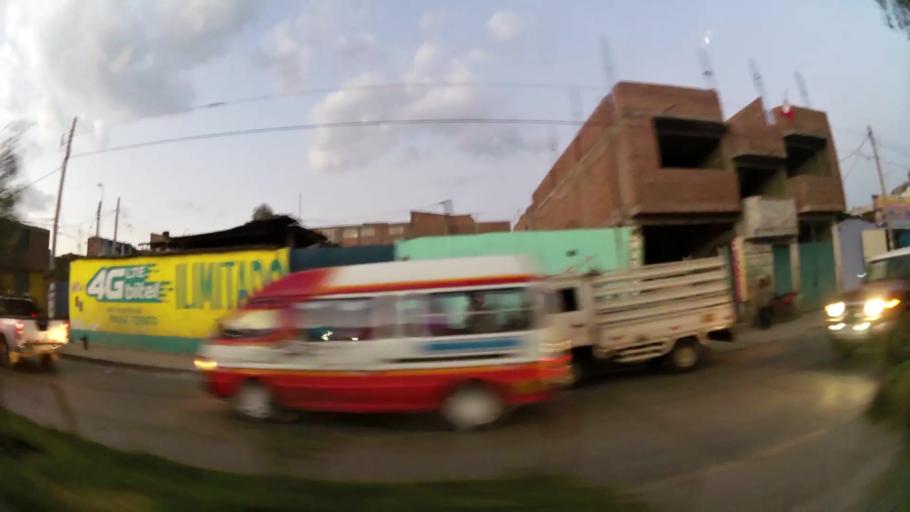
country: PE
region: Junin
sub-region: Provincia de Huancayo
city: El Tambo
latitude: -12.0576
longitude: -75.2225
